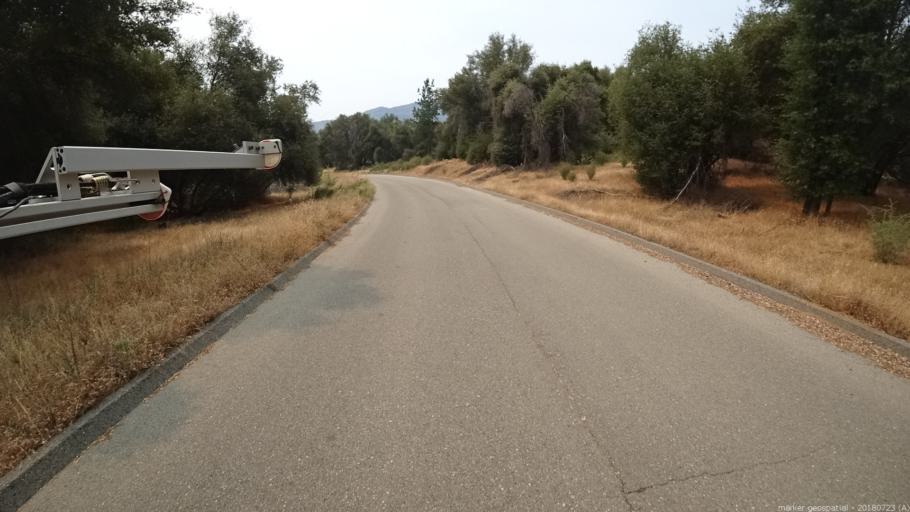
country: US
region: California
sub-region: Madera County
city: Oakhurst
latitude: 37.3454
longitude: -119.6684
